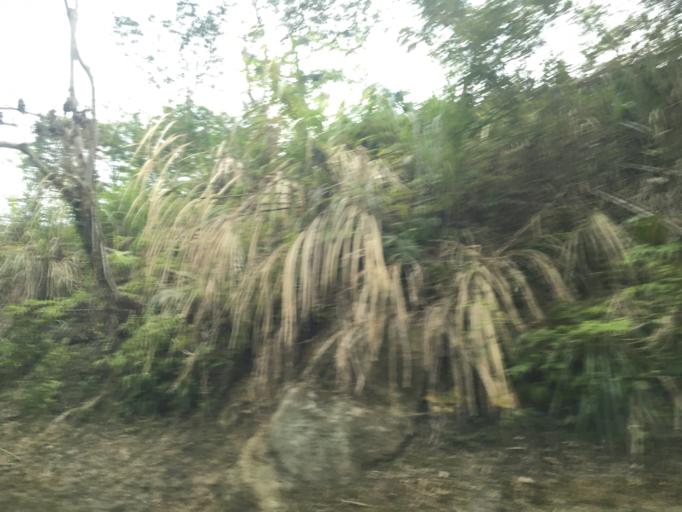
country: TW
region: Taiwan
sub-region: Nantou
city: Puli
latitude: 23.9470
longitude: 120.8474
